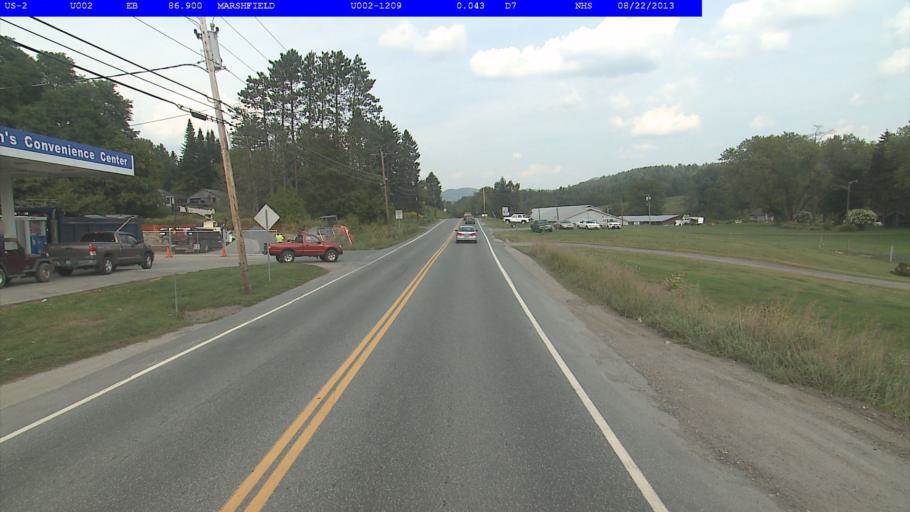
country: US
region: Vermont
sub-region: Washington County
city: Barre
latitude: 44.2800
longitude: -72.4214
